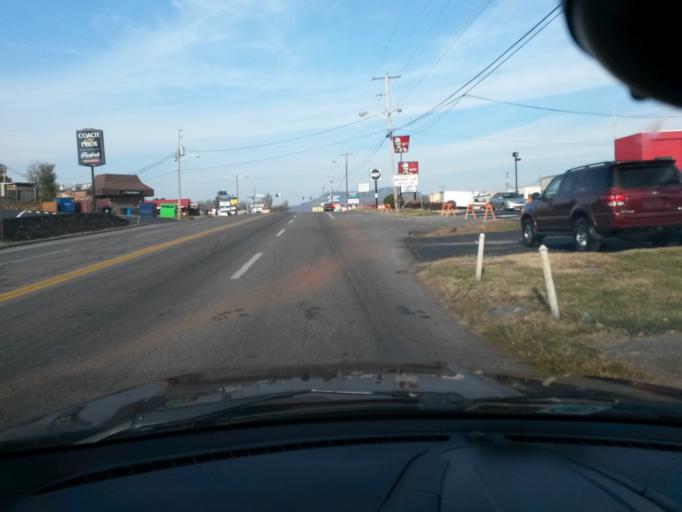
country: US
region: Virginia
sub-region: Roanoke County
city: Hollins
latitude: 37.3206
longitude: -79.9546
